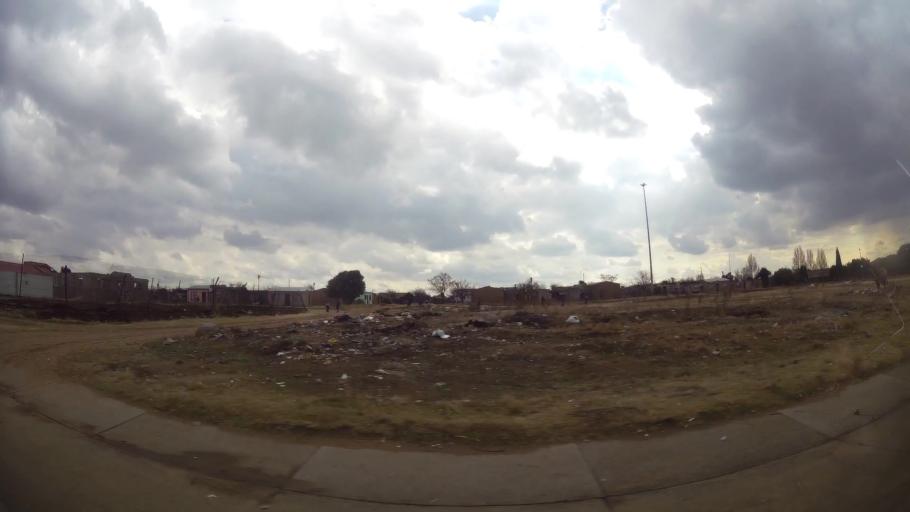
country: ZA
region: Orange Free State
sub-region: Fezile Dabi District Municipality
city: Sasolburg
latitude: -26.8525
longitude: 27.8773
